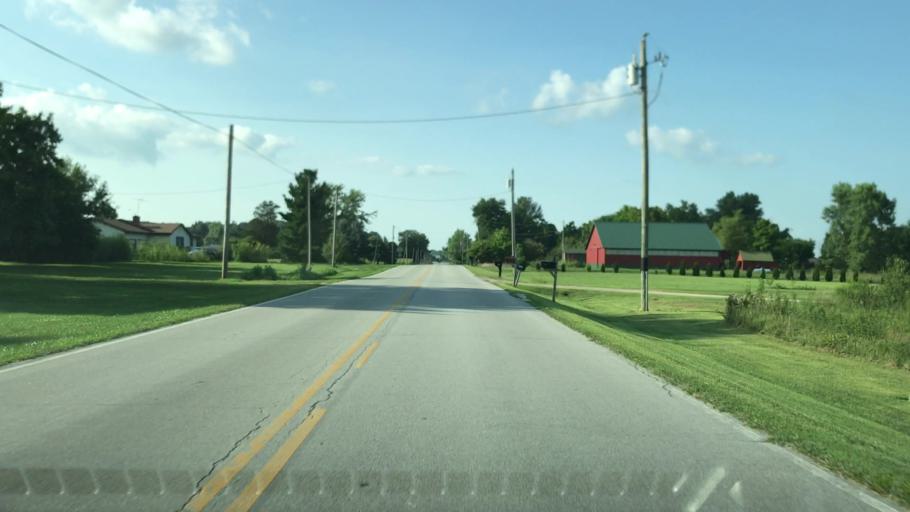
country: US
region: Ohio
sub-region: Union County
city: Marysville
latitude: 40.2092
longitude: -83.3539
